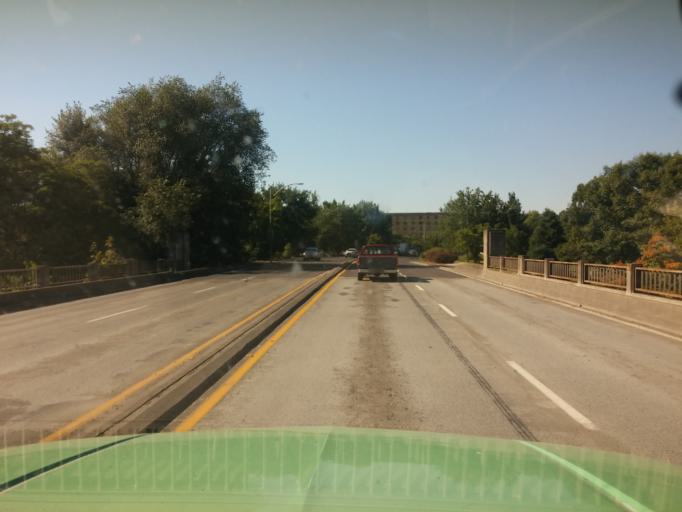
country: US
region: Idaho
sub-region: Nez Perce County
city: Lewiston
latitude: 46.4172
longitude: -117.0002
